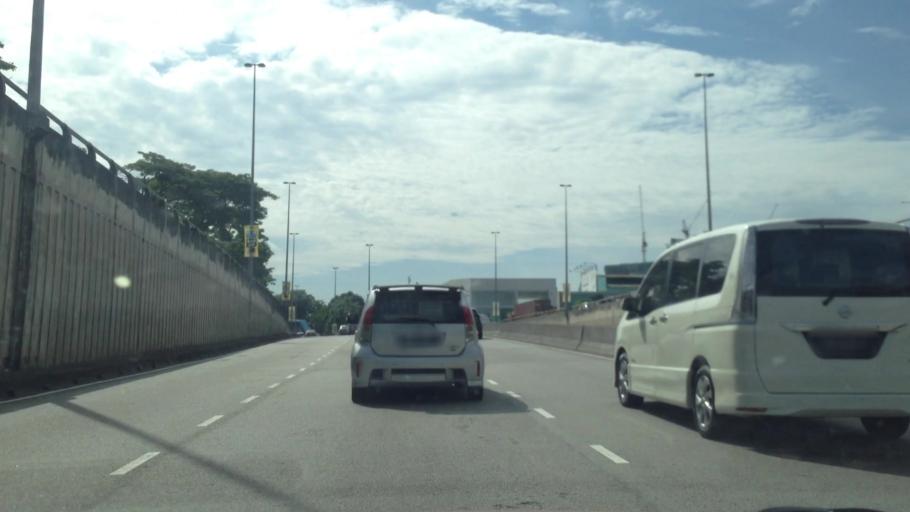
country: MY
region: Selangor
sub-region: Petaling
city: Petaling Jaya
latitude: 3.0746
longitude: 101.6153
